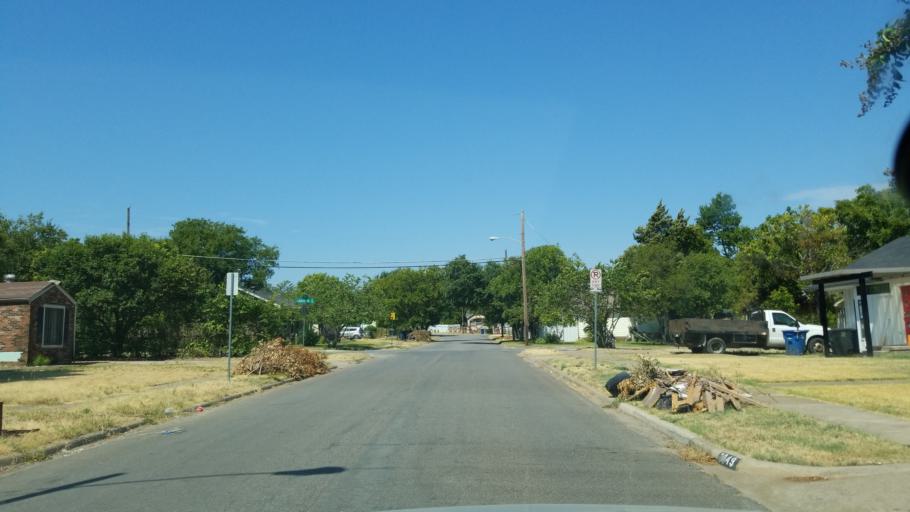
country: US
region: Texas
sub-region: Dallas County
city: Cockrell Hill
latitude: 32.7453
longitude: -96.8826
